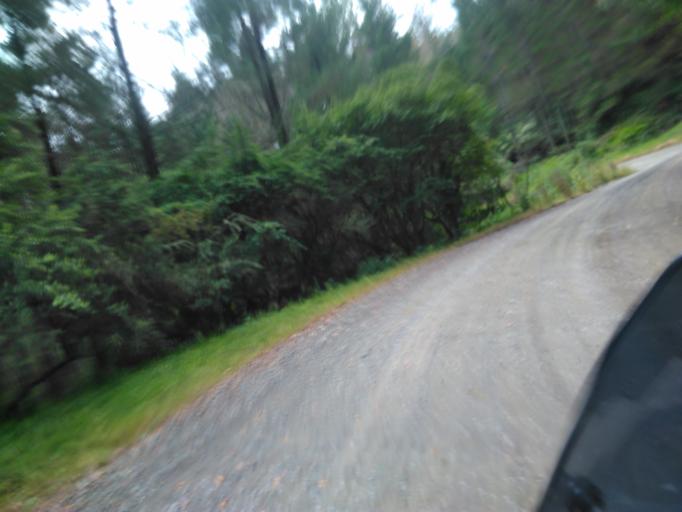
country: NZ
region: Gisborne
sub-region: Gisborne District
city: Gisborne
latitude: -38.0583
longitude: 178.1393
